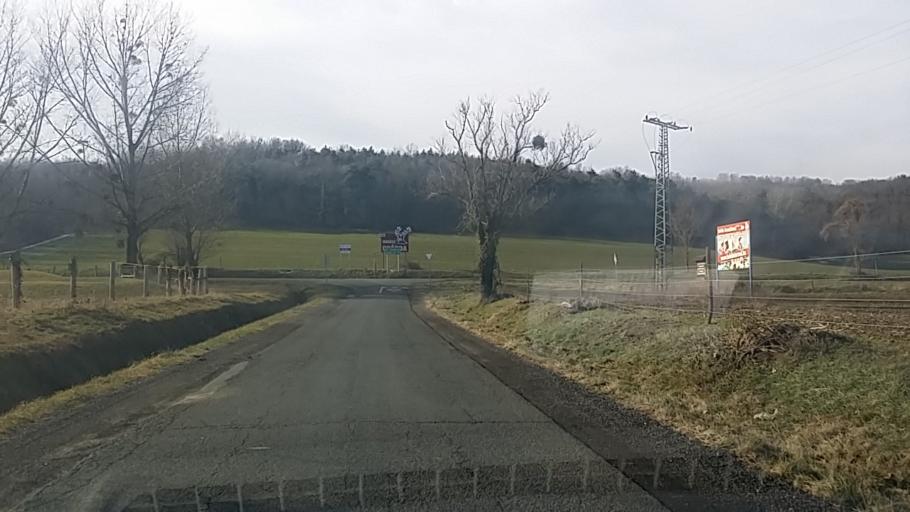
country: HU
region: Zala
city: Heviz
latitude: 46.8289
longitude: 17.0936
